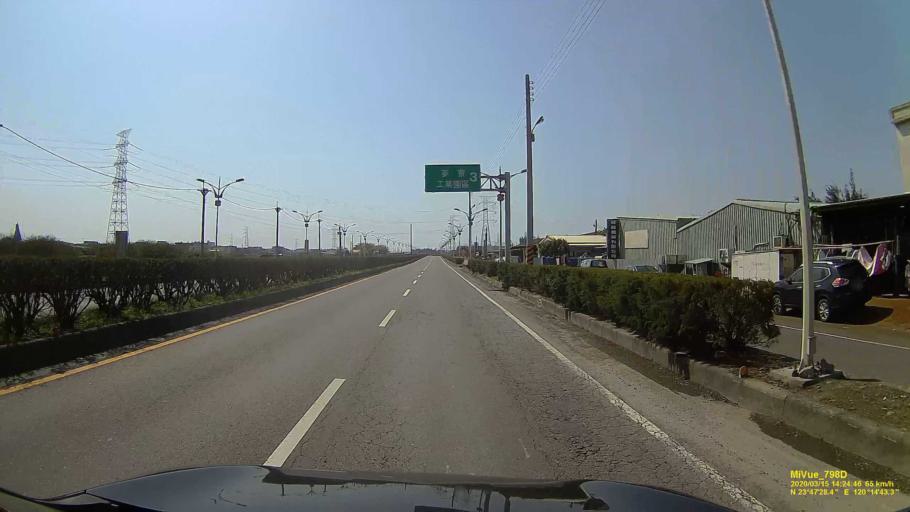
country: TW
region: Taiwan
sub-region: Yunlin
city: Douliu
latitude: 23.7912
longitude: 120.2450
